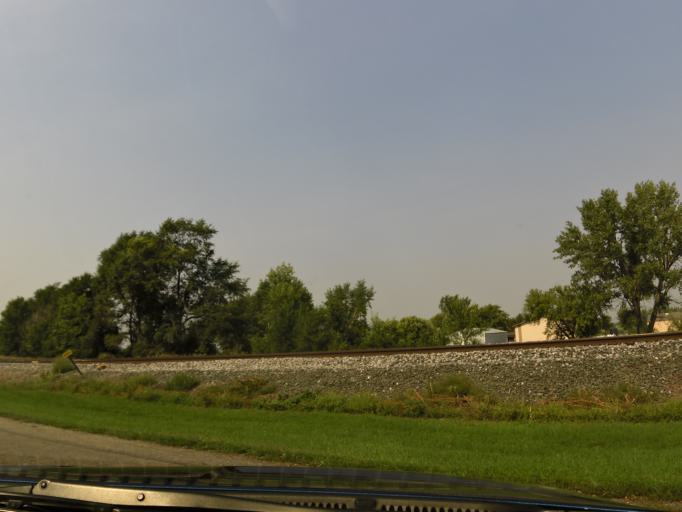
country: US
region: South Dakota
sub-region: Roberts County
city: Sisseton
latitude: 46.0785
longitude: -97.1446
